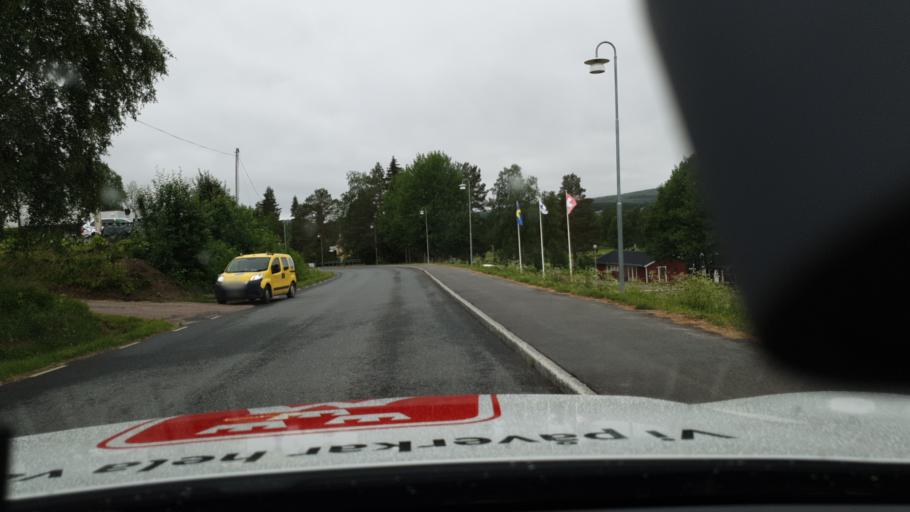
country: SE
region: Norrbotten
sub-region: Overtornea Kommun
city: OEvertornea
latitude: 66.3946
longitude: 23.6486
